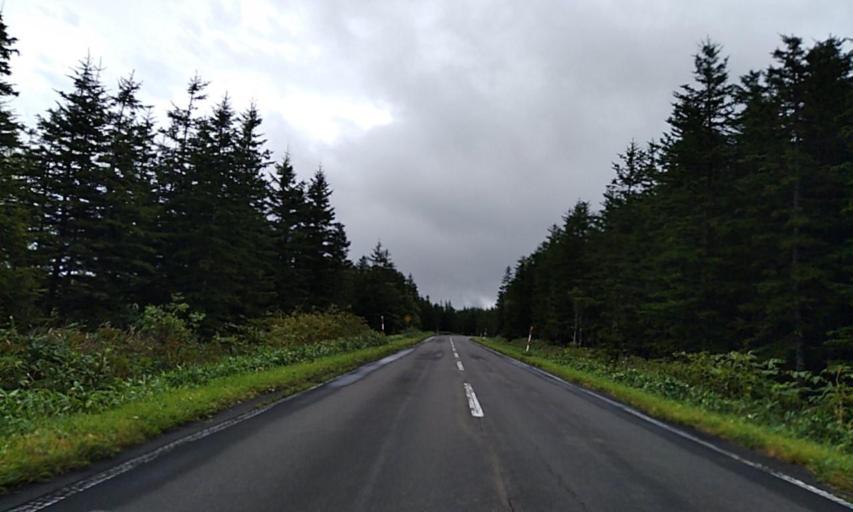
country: JP
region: Hokkaido
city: Abashiri
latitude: 43.6109
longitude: 144.5921
